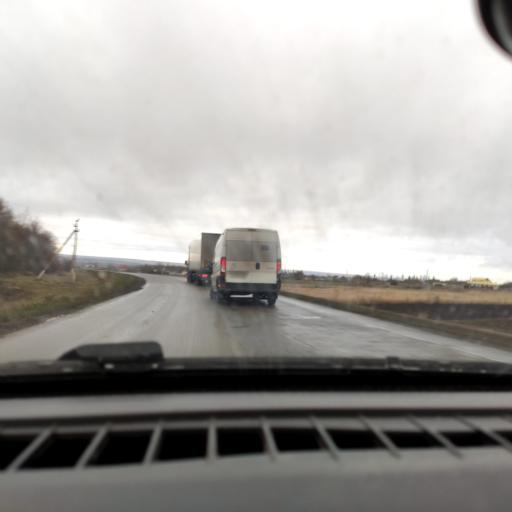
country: RU
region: Belgorod
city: Ilovka
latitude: 50.7237
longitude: 38.6808
